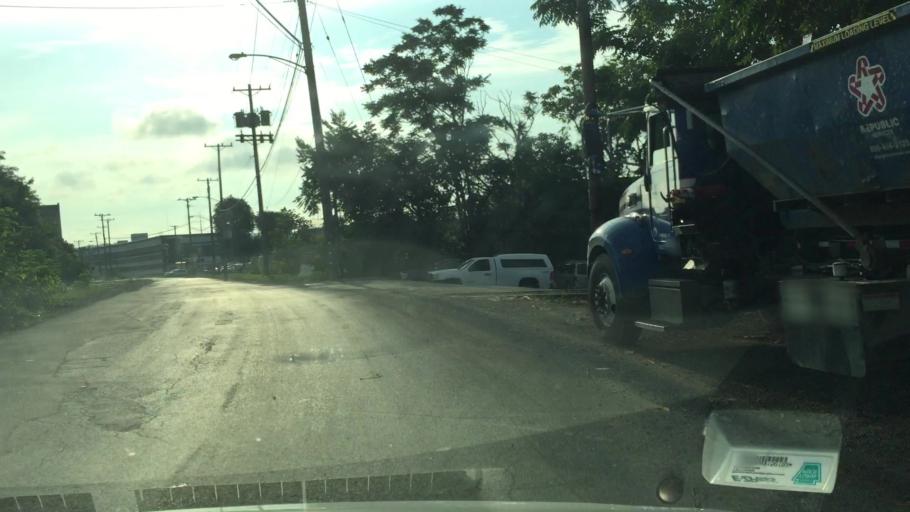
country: US
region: Pennsylvania
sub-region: Allegheny County
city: McKees Rocks
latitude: 40.4632
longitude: -80.0683
